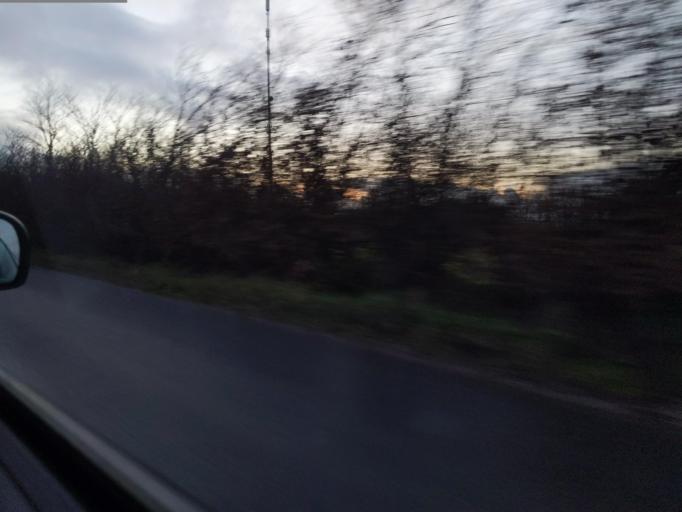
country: GB
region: England
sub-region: Devon
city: Great Torrington
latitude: 50.9810
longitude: -4.0945
